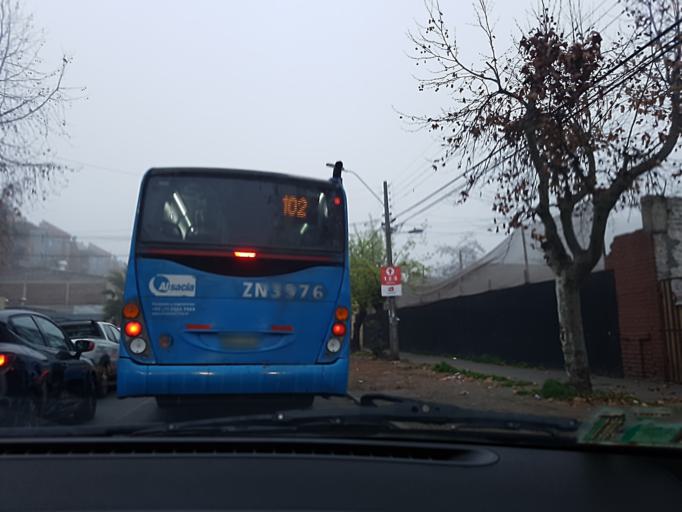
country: CL
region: Santiago Metropolitan
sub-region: Provincia de Santiago
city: Lo Prado
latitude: -33.4566
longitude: -70.6953
